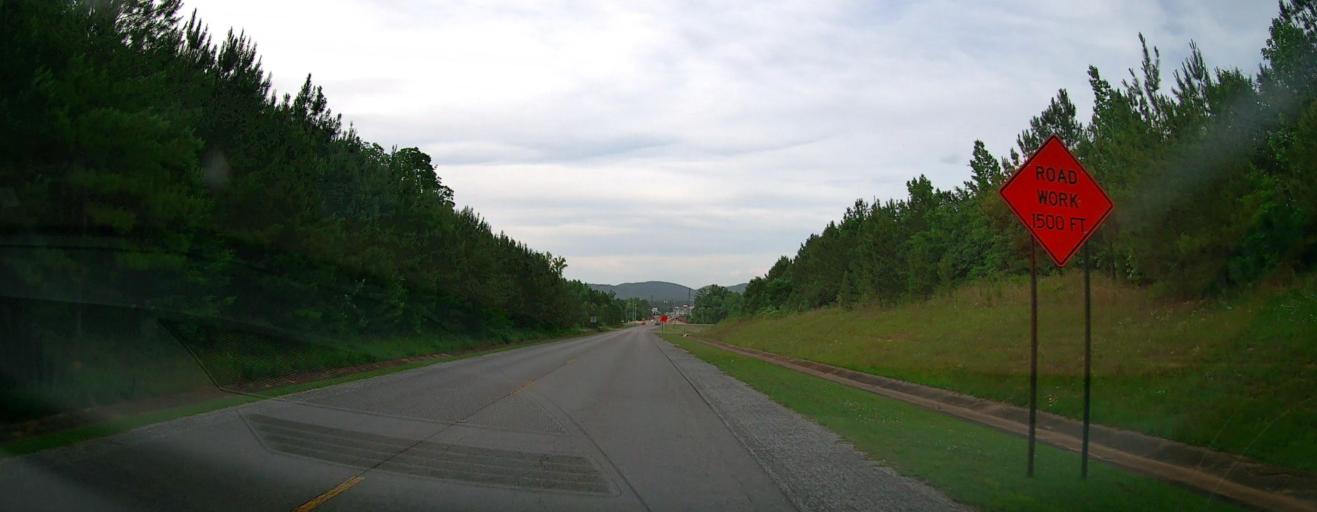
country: US
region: Alabama
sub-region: Calhoun County
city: Oxford
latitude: 33.5963
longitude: -85.7858
